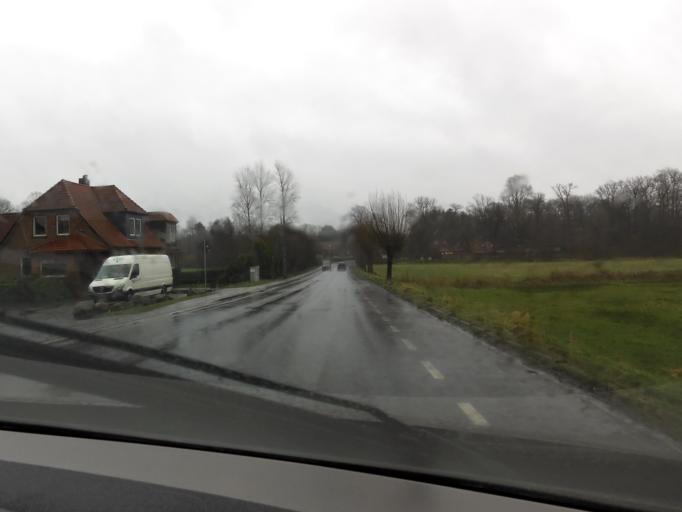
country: DE
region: Lower Saxony
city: Bad Fallingbostel
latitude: 52.8988
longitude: 9.7597
